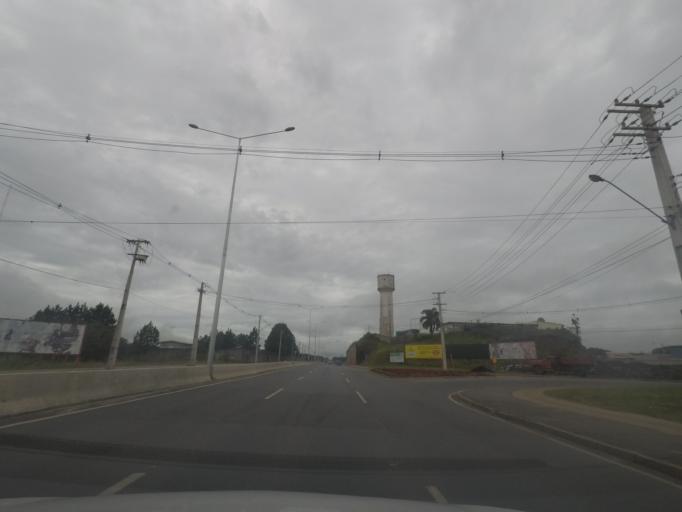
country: BR
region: Parana
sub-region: Piraquara
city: Piraquara
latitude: -25.4496
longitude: -49.1273
